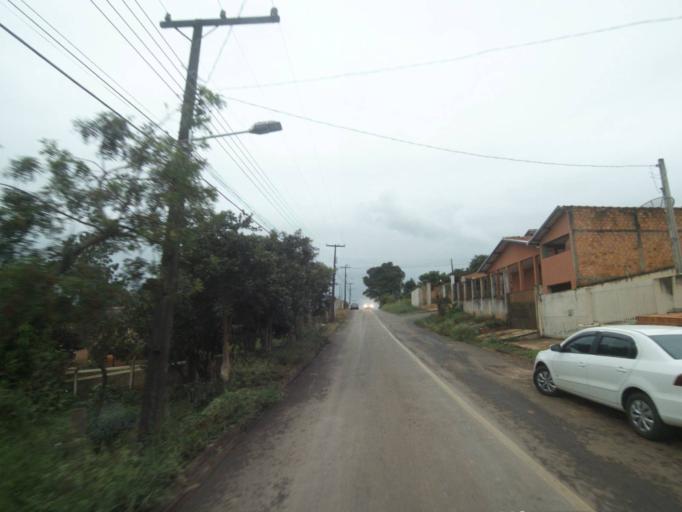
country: BR
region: Parana
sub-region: Telemaco Borba
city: Telemaco Borba
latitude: -24.3180
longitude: -50.6538
